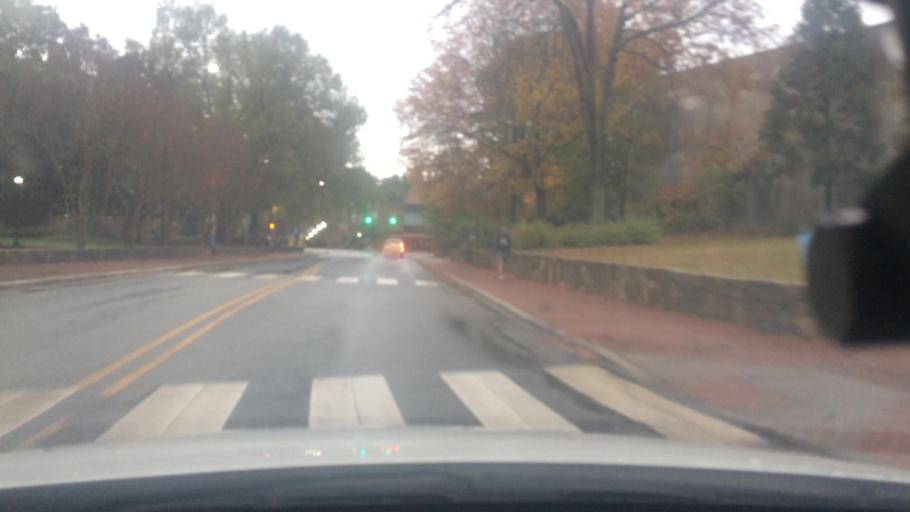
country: US
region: North Carolina
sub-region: Orange County
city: Chapel Hill
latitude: 35.9110
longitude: -79.0468
